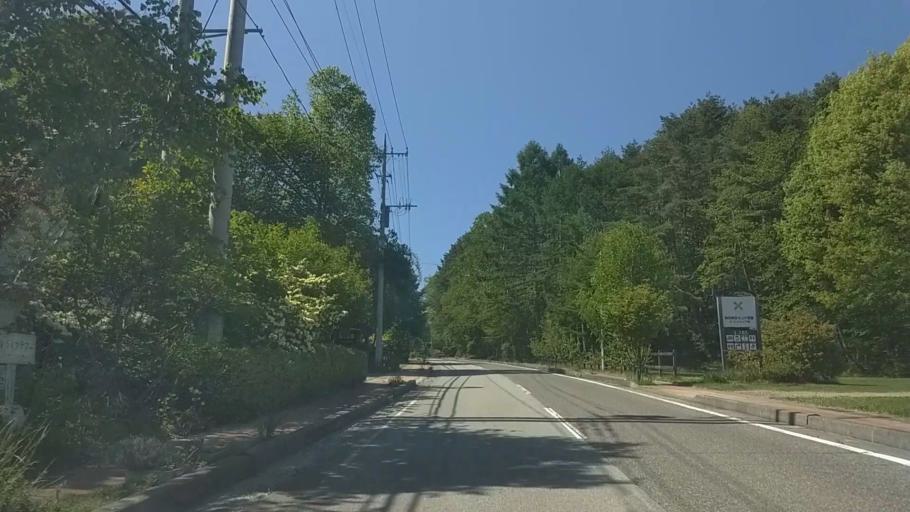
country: JP
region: Yamanashi
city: Nirasaki
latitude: 35.8998
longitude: 138.4365
